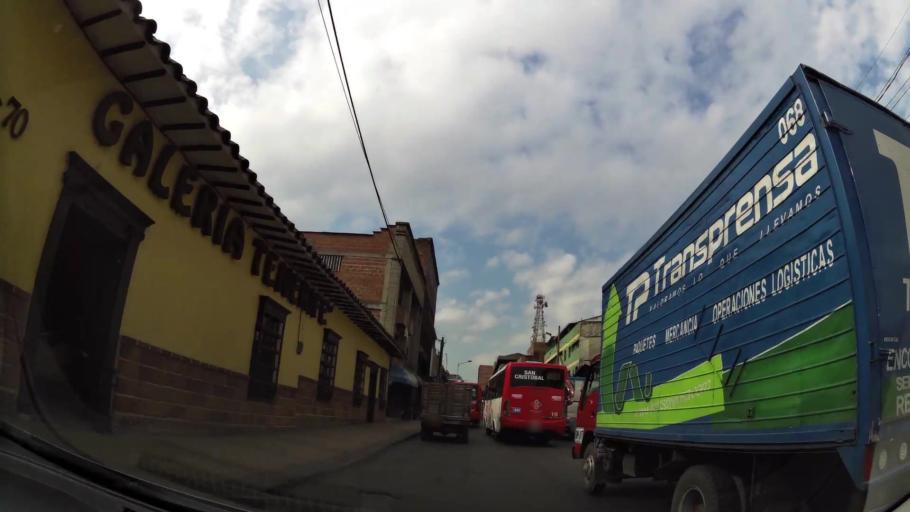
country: CO
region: Antioquia
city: Medellin
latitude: 6.2528
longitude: -75.5714
